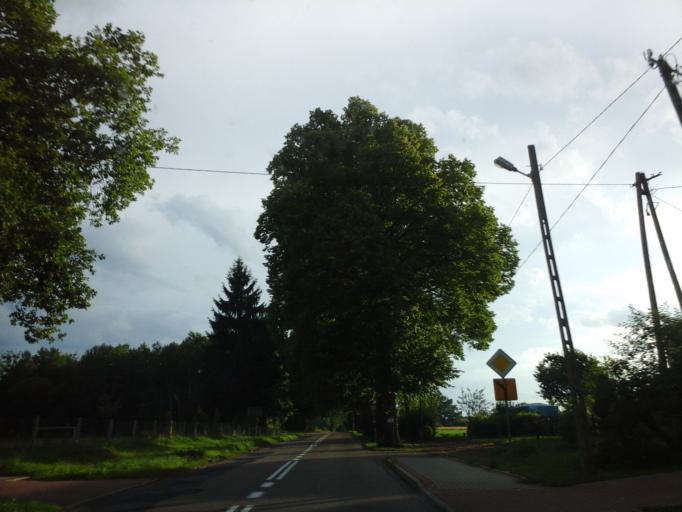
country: PL
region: West Pomeranian Voivodeship
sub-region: Powiat kamienski
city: Golczewo
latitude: 53.7505
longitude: 15.0133
